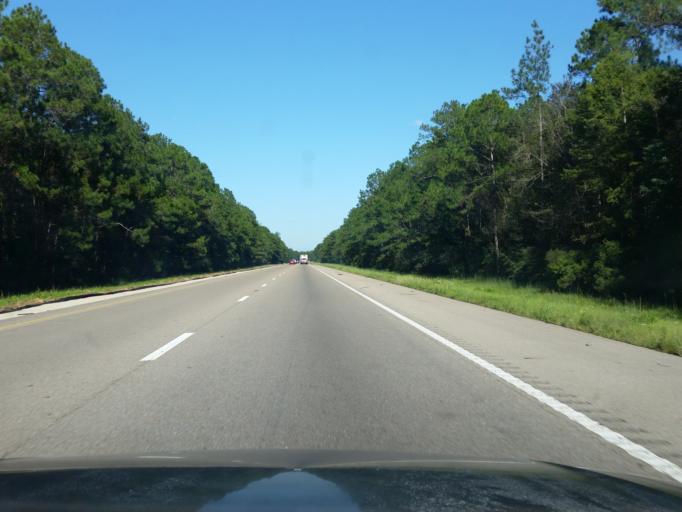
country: US
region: Mississippi
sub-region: Hancock County
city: Pearlington
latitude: 30.3284
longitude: -89.5558
